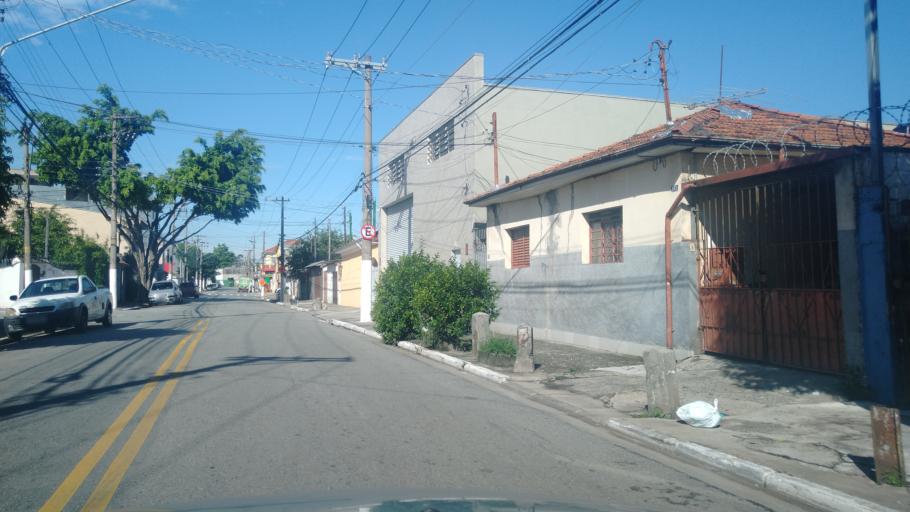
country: BR
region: Sao Paulo
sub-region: Sao Paulo
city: Sao Paulo
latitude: -23.5188
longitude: -46.6041
